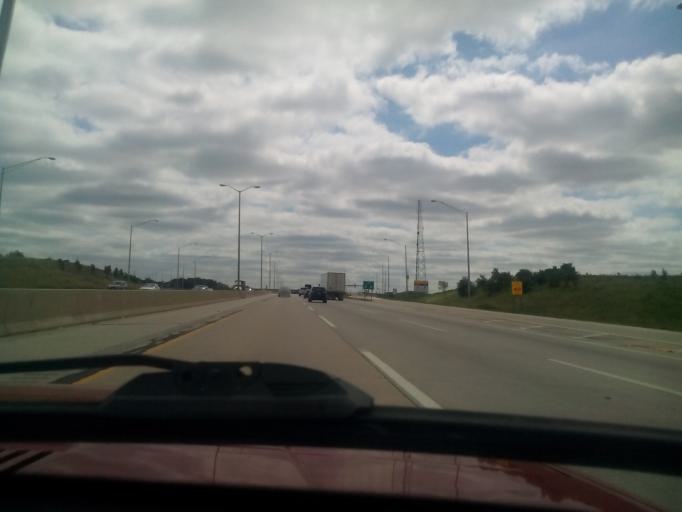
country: US
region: Illinois
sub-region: Cook County
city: Lemont
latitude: 41.6619
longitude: -88.0230
